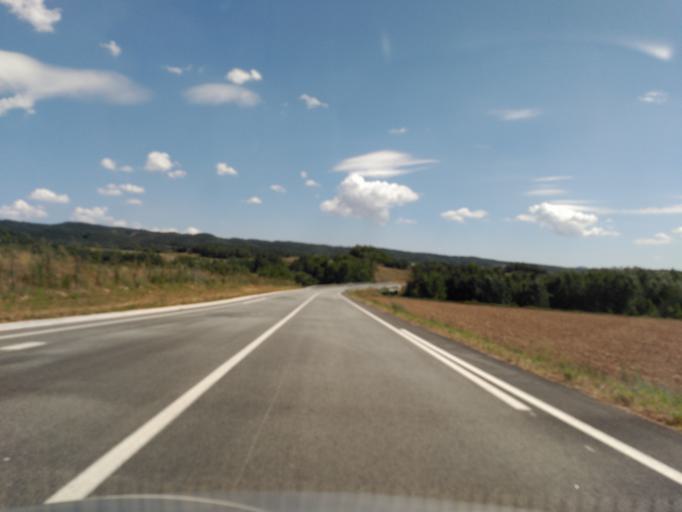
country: ES
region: Catalonia
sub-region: Provincia de Barcelona
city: Olost
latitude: 41.9892
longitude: 2.1018
